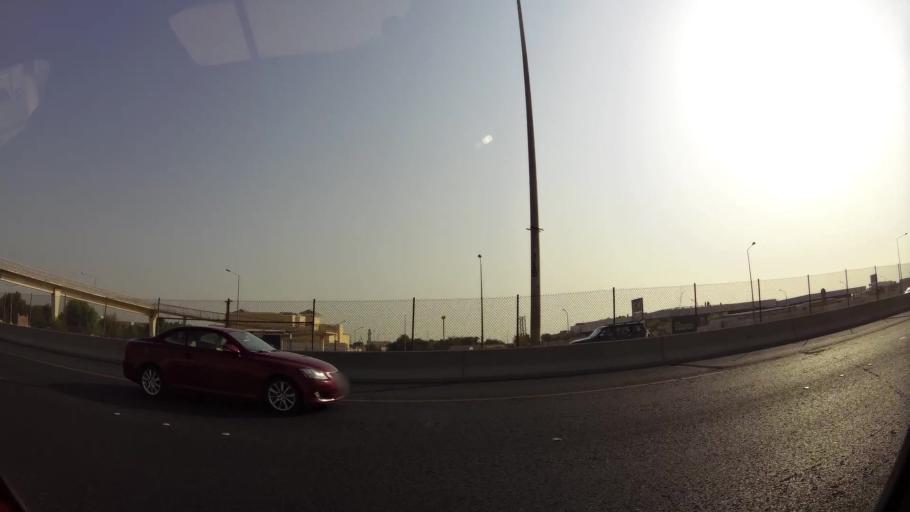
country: KW
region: Mubarak al Kabir
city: Mubarak al Kabir
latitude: 29.1956
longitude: 48.1083
